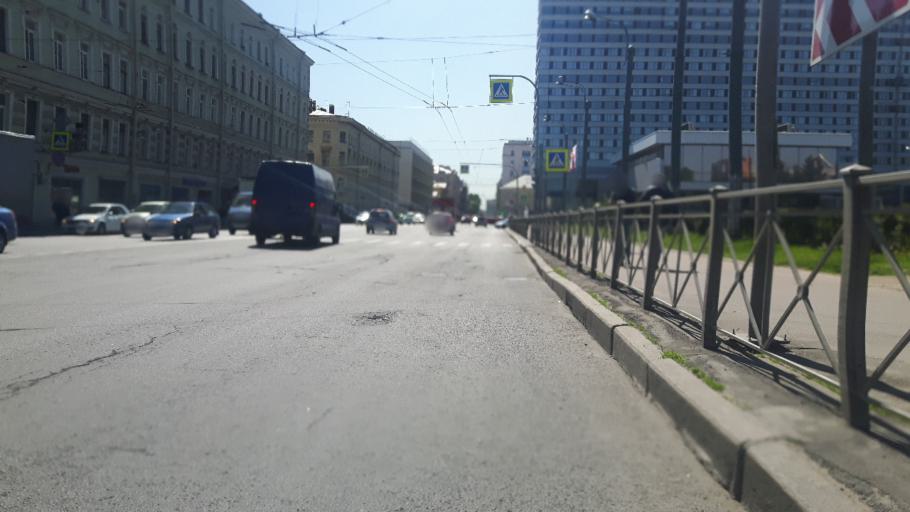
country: RU
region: St.-Petersburg
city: Admiralteisky
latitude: 59.9160
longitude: 30.2972
